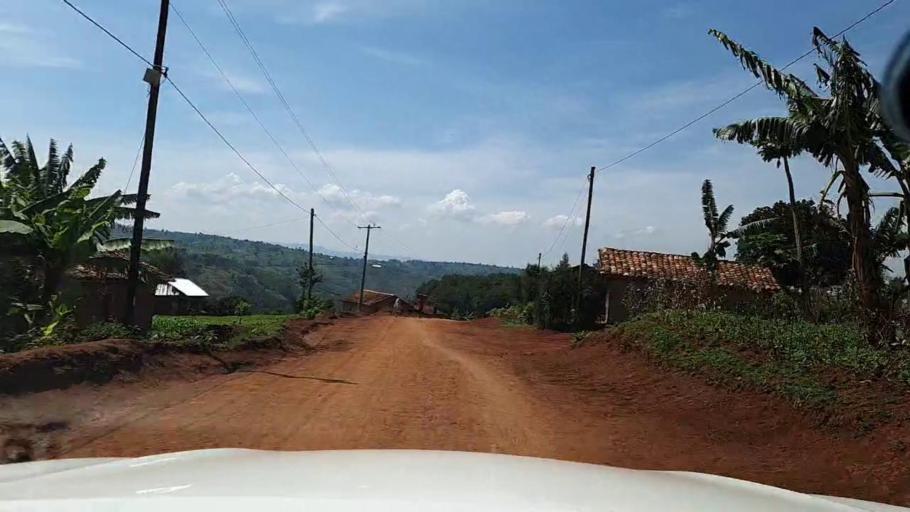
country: RW
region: Southern Province
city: Butare
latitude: -2.7133
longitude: 29.8397
